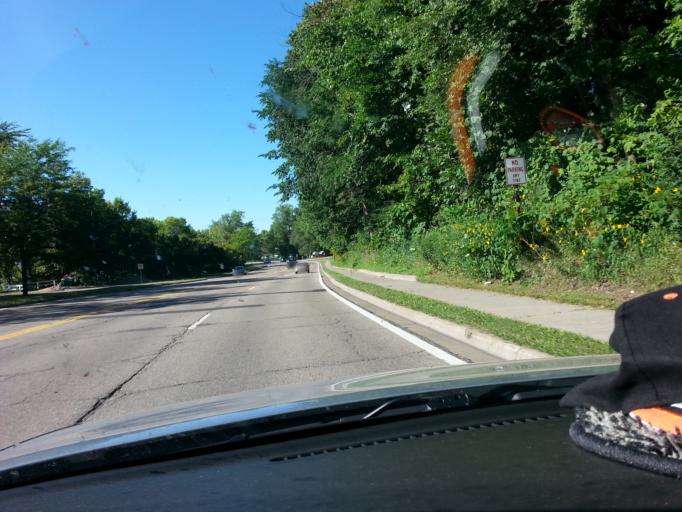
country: US
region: Minnesota
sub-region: Scott County
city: Prior Lake
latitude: 44.7167
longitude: -93.4338
